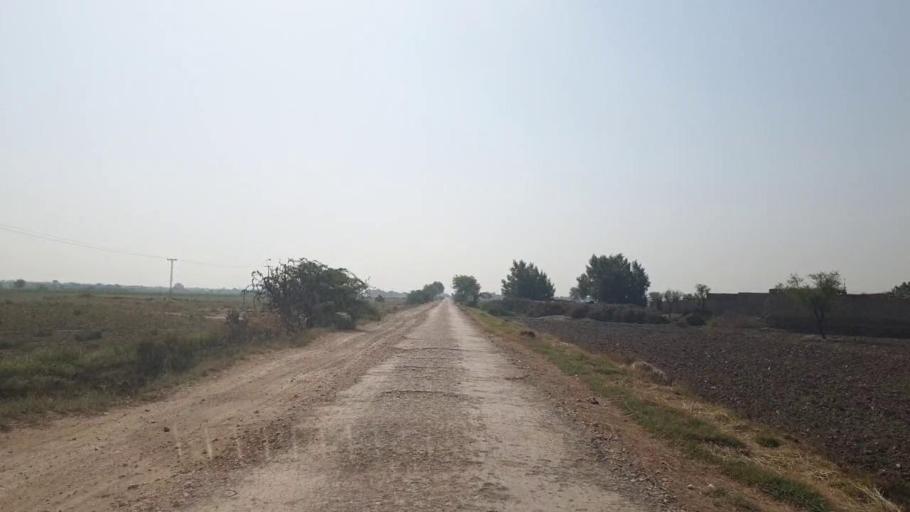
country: PK
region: Sindh
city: Shahdadpur
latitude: 25.9020
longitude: 68.7460
